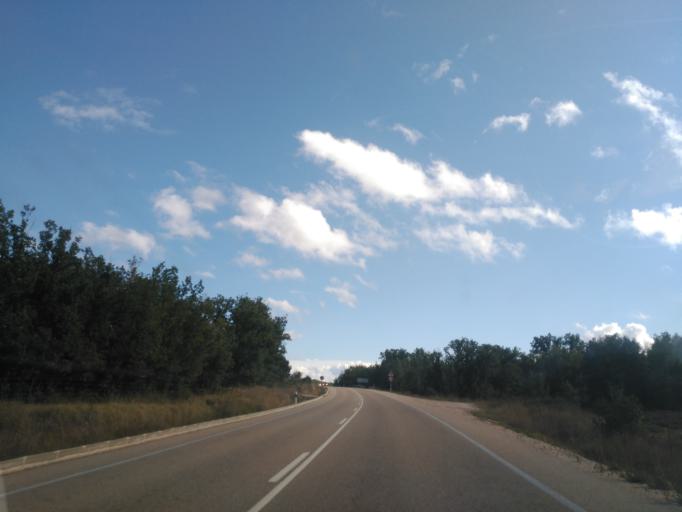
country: ES
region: Castille and Leon
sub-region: Provincia de Burgos
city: Pinilla de los Barruecos
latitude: 41.9295
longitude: -3.2822
